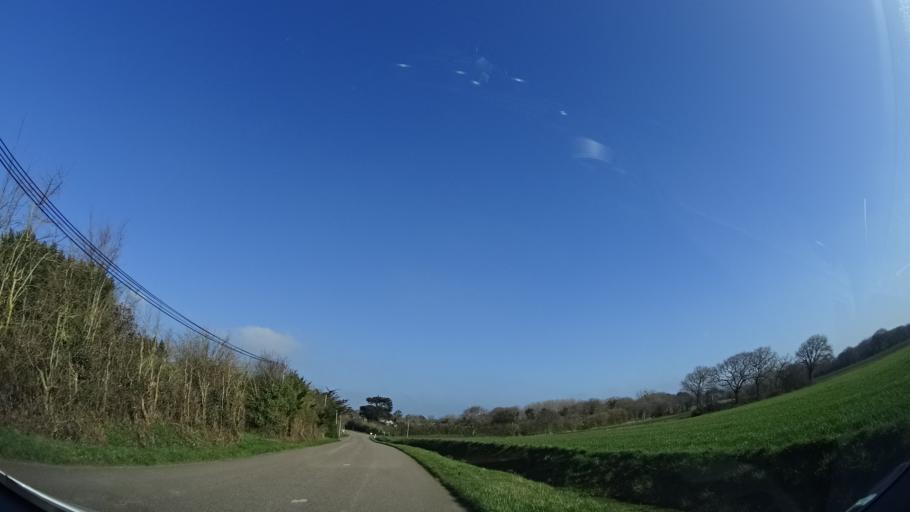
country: FR
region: Brittany
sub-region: Departement des Cotes-d'Armor
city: Matignon
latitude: 48.6575
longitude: -2.3269
